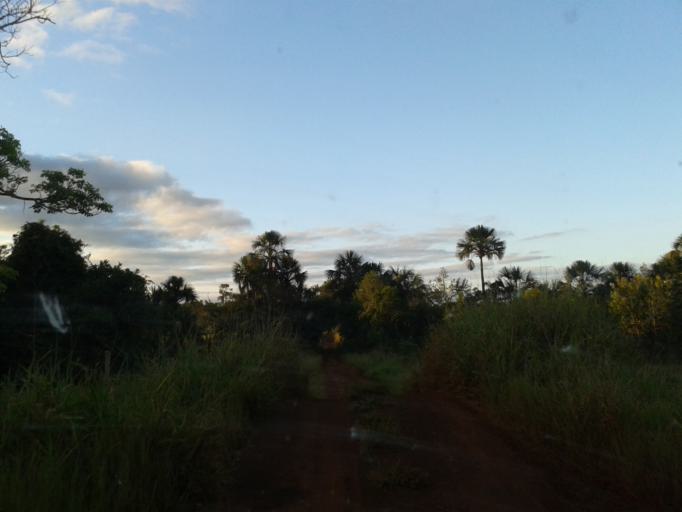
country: BR
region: Minas Gerais
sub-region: Campina Verde
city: Campina Verde
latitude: -19.5028
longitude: -49.6818
